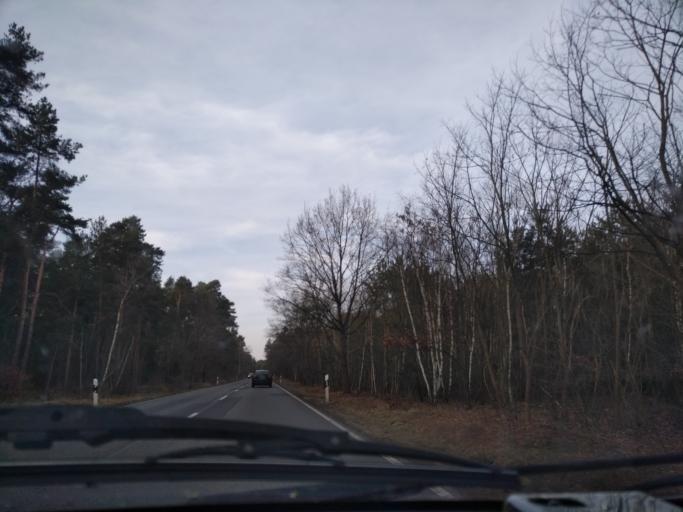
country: DE
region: Saxony-Anhalt
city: Holzdorf
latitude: 51.7753
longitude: 13.1965
